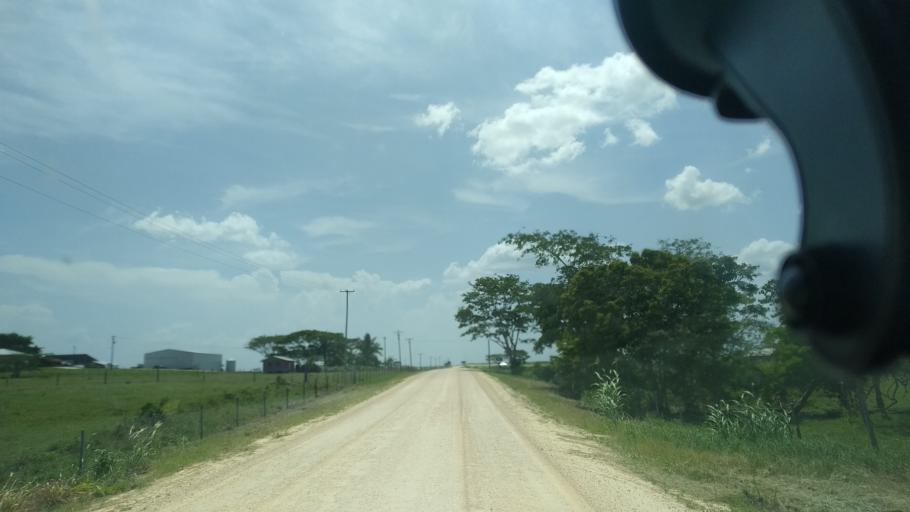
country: BZ
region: Cayo
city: San Ignacio
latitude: 17.3148
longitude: -89.0396
